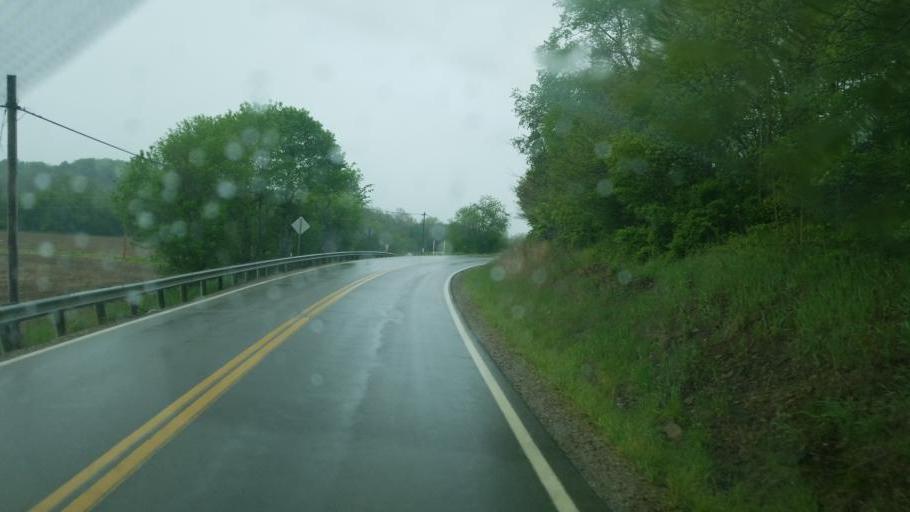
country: US
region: Ohio
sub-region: Muskingum County
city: Dresden
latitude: 40.2011
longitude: -82.0496
